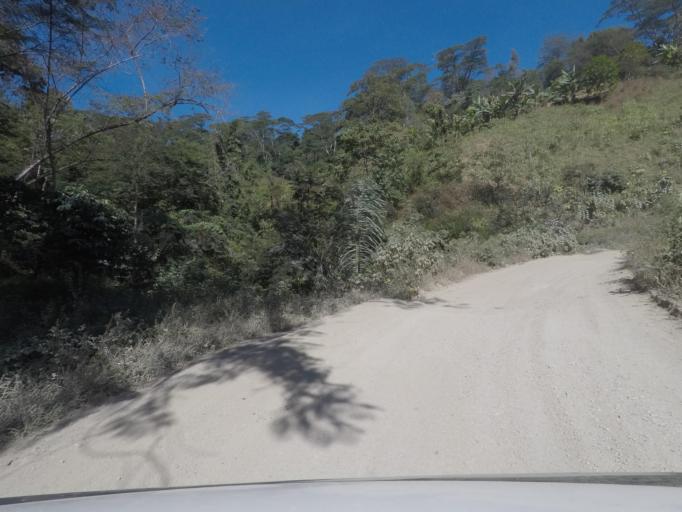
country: TL
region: Ermera
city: Gleno
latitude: -8.7561
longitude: 125.4326
